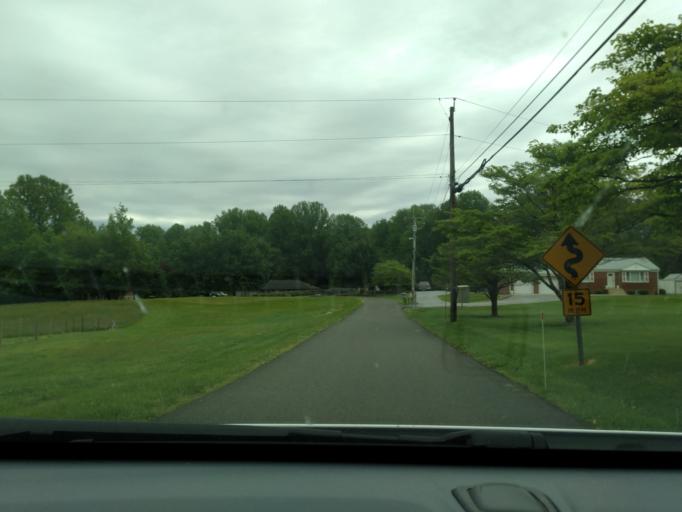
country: US
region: Maryland
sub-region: Prince George's County
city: Marlboro Meadows
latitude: 38.8544
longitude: -76.7166
